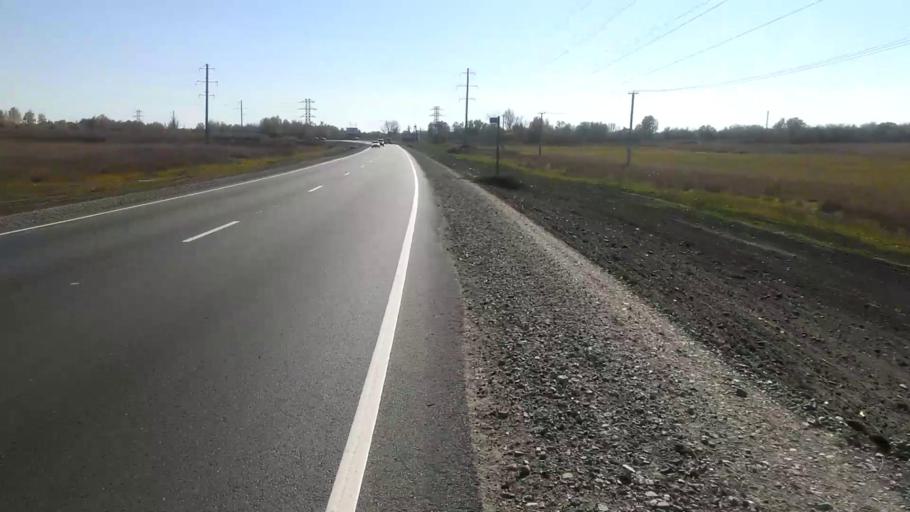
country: RU
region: Altai Krai
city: Sannikovo
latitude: 53.3326
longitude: 83.9379
